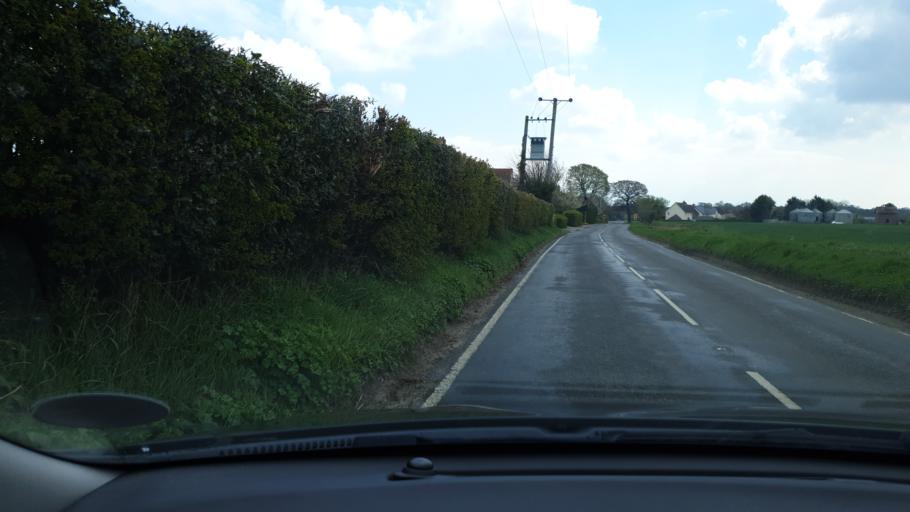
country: GB
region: England
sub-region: Essex
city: Alresford
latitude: 51.8970
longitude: 1.0217
